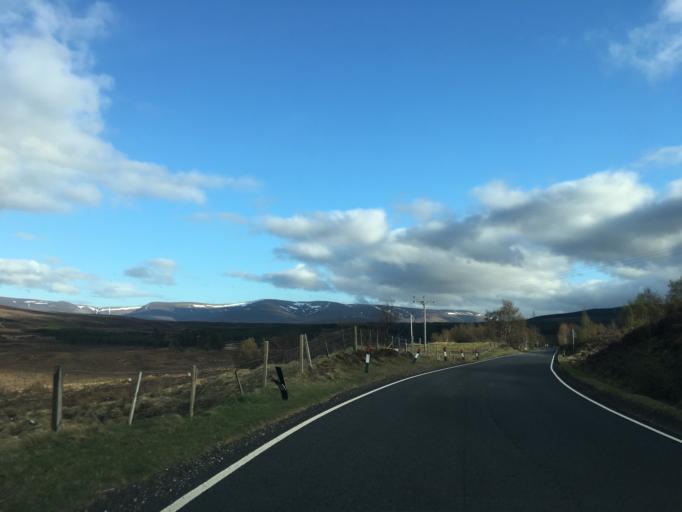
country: GB
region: Scotland
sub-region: Highland
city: Kingussie
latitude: 56.9969
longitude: -4.2485
